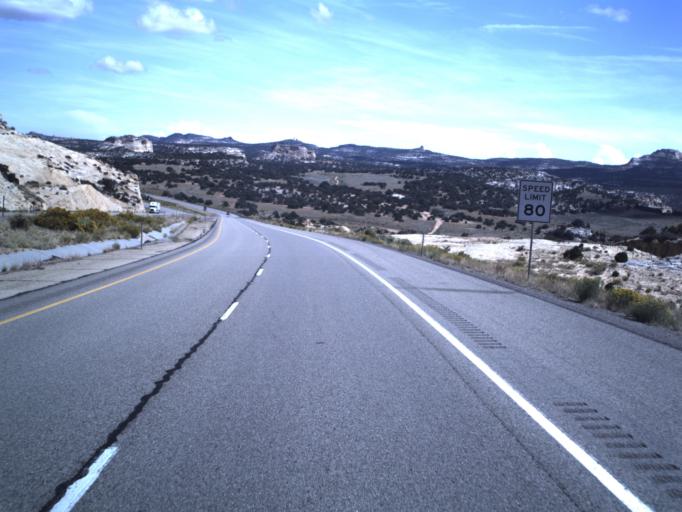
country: US
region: Utah
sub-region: Emery County
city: Ferron
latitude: 38.8485
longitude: -110.9020
